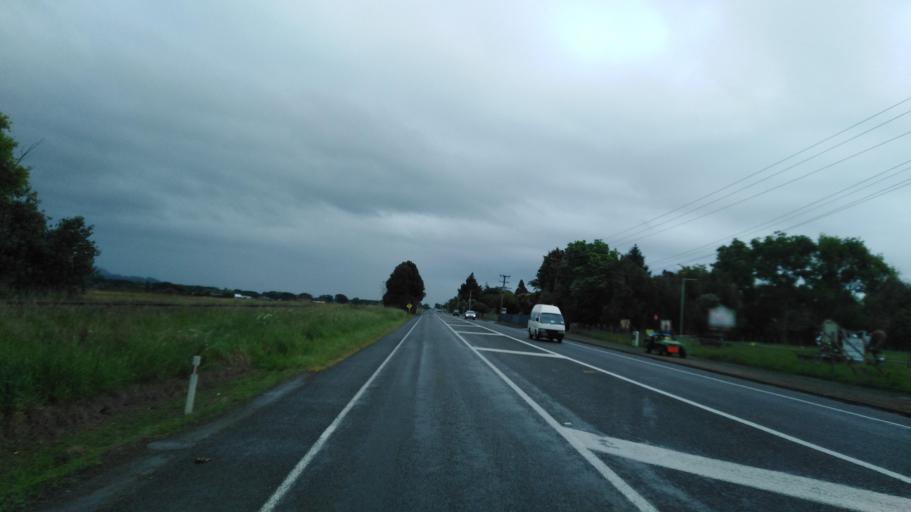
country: NZ
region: Manawatu-Wanganui
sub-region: Horowhenua District
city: Levin
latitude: -40.6407
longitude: 175.2680
